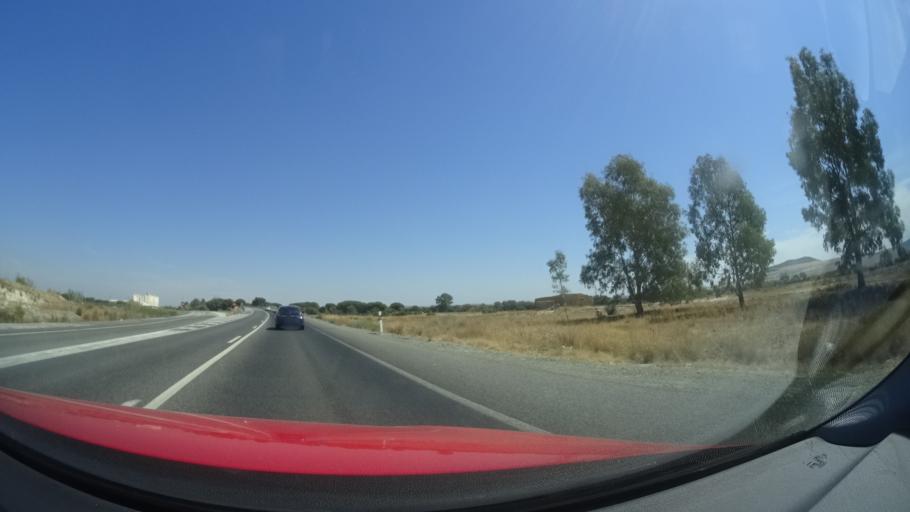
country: ES
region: Andalusia
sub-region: Provincia de Sevilla
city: Las Cabezas de San Juan
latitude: 36.9057
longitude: -5.9741
